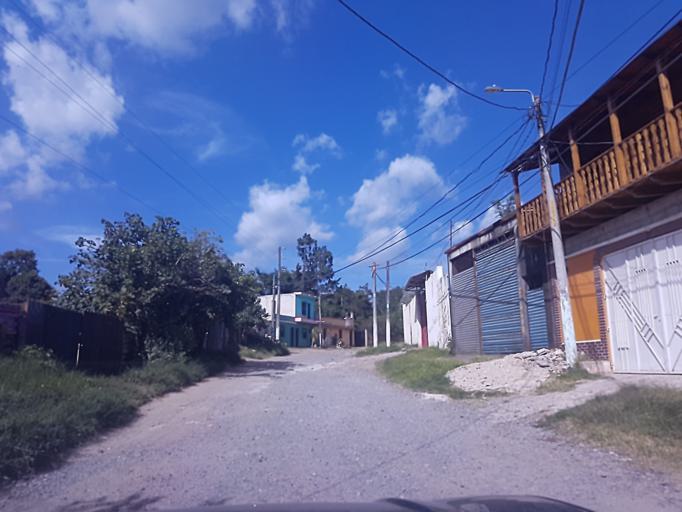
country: GT
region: Guatemala
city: Petapa
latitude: 14.5041
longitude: -90.5587
